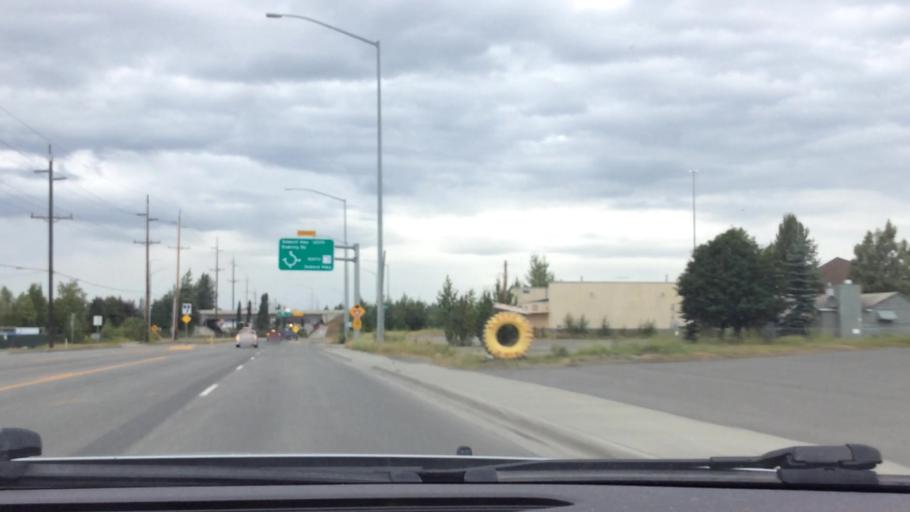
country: US
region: Alaska
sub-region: Anchorage Municipality
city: Anchorage
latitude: 61.1665
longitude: -149.8516
